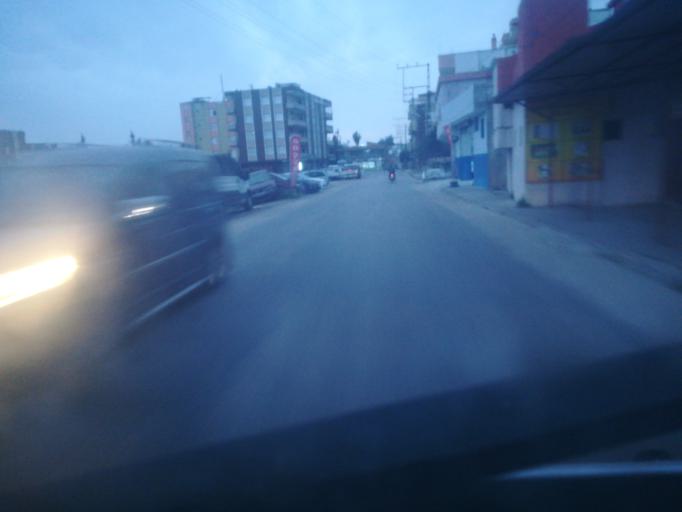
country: TR
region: Adana
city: Seyhan
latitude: 37.0142
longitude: 35.2838
